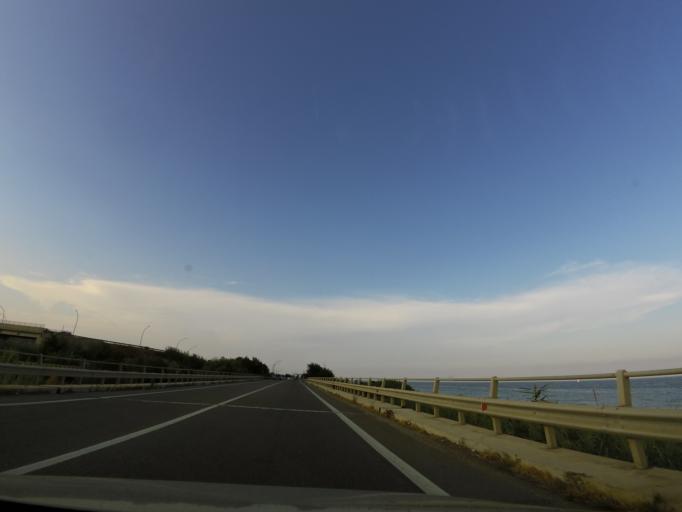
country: IT
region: Calabria
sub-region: Provincia di Reggio Calabria
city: Monasterace Marina
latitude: 38.4264
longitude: 16.5695
